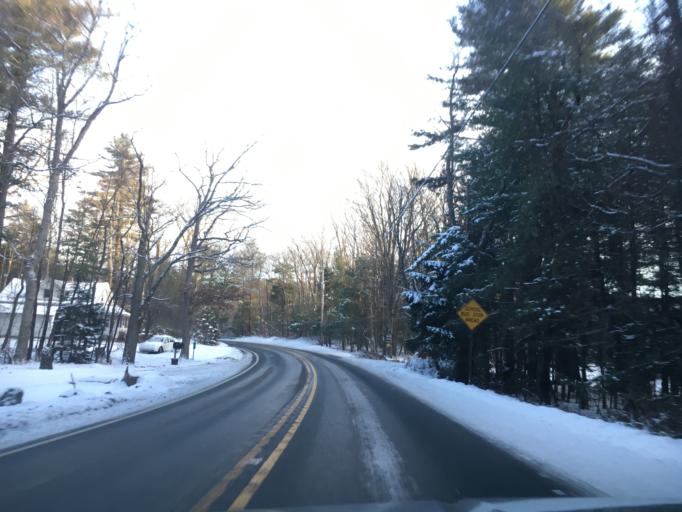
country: US
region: Pennsylvania
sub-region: Pike County
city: Hemlock Farms
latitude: 41.3223
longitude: -75.1189
